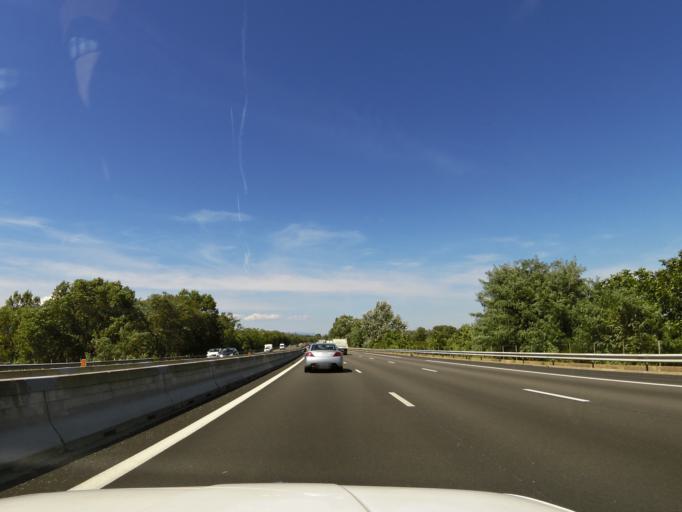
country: FR
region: Rhone-Alpes
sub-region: Departement de la Drome
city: La Roche-de-Glun
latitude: 44.9916
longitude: 4.8808
